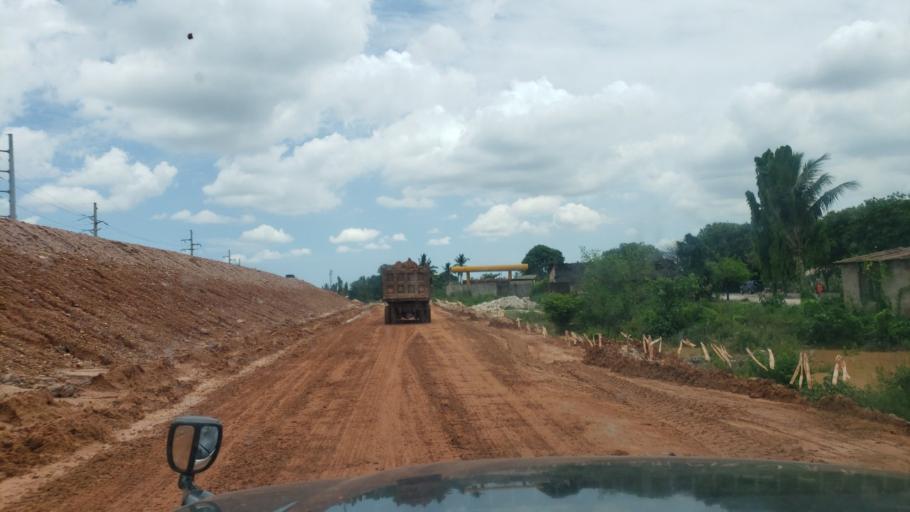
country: TZ
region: Pwani
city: Kisarawe
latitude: -6.8846
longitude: 39.1496
